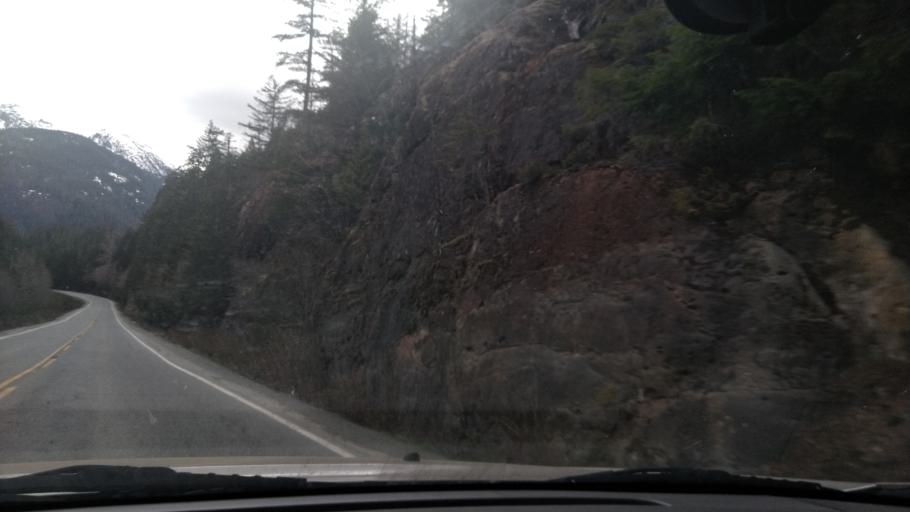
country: CA
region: British Columbia
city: Campbell River
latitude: 49.8457
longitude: -125.8574
